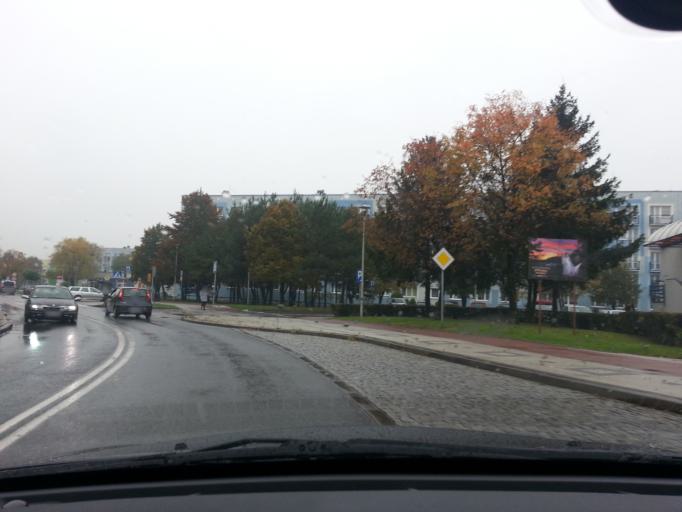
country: PL
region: Silesian Voivodeship
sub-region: Powiat gliwicki
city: Knurow
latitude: 50.2325
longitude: 18.6594
